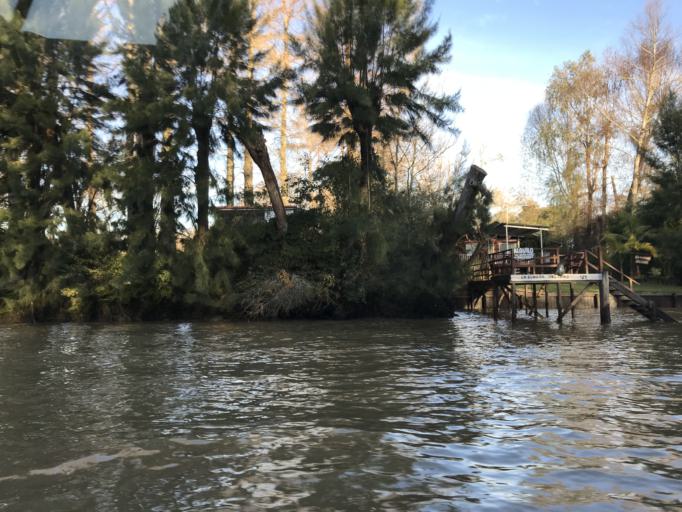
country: AR
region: Buenos Aires
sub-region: Partido de Tigre
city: Tigre
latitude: -34.3736
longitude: -58.5858
